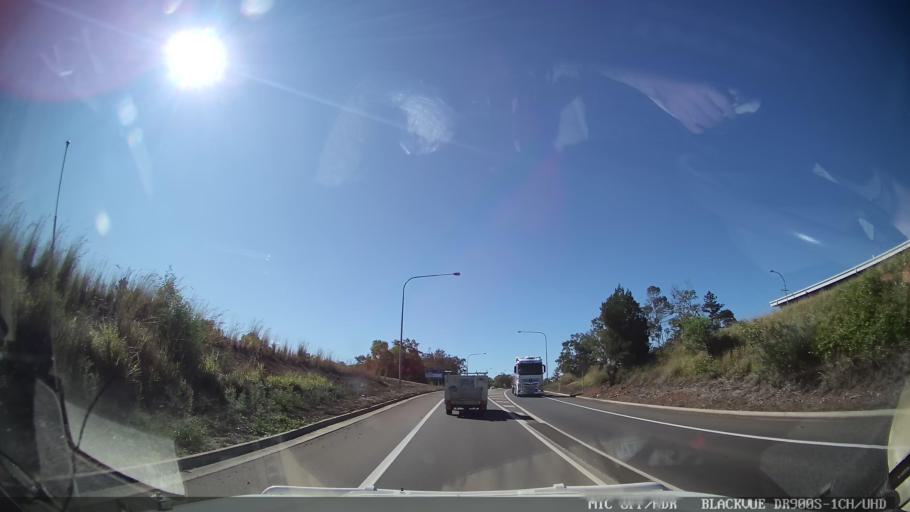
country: AU
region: Queensland
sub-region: Fraser Coast
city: Maryborough
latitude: -25.5164
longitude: 152.6702
